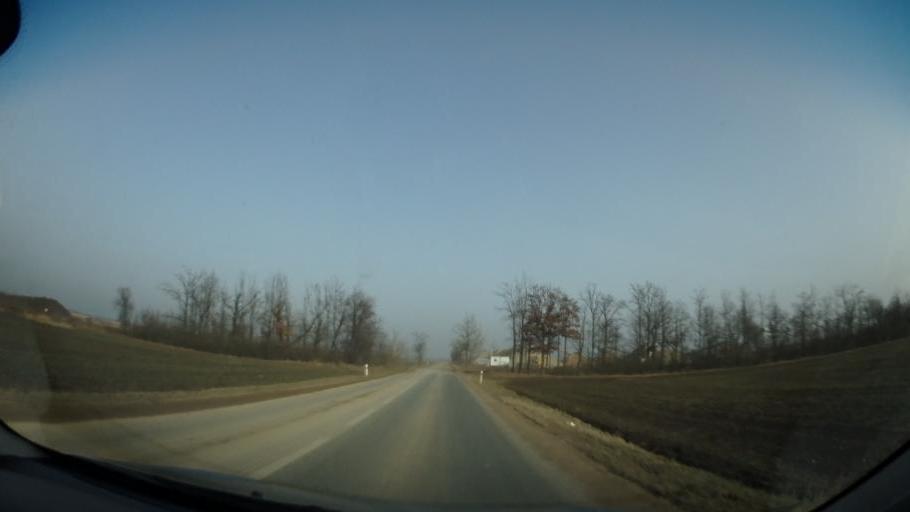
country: CZ
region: South Moravian
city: Hrusovany u Brna
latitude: 49.0391
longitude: 16.5468
